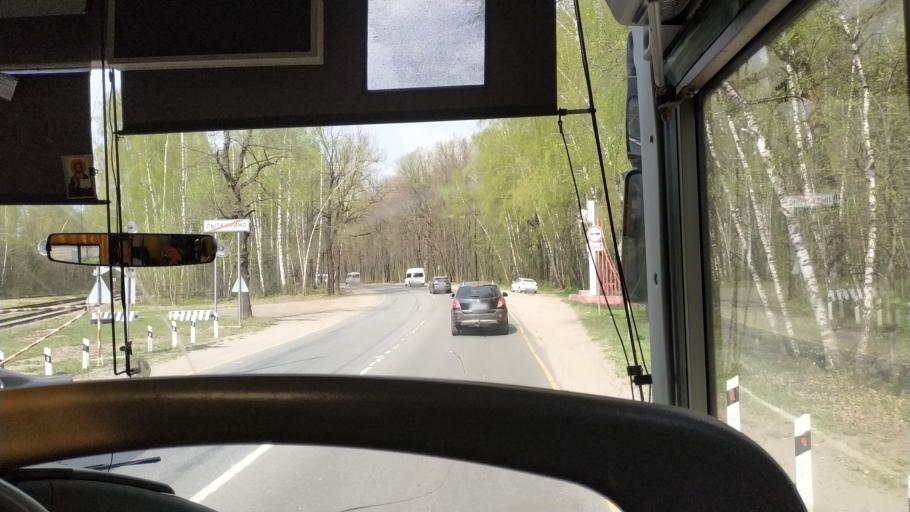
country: RU
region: Moskovskaya
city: Lytkarino
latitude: 55.5922
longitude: 37.9150
